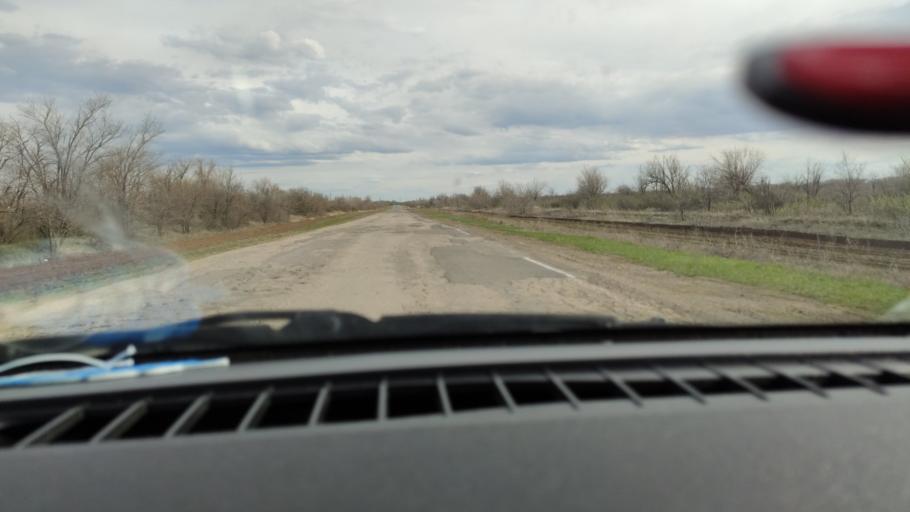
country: RU
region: Saratov
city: Rovnoye
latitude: 50.9483
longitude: 46.1245
